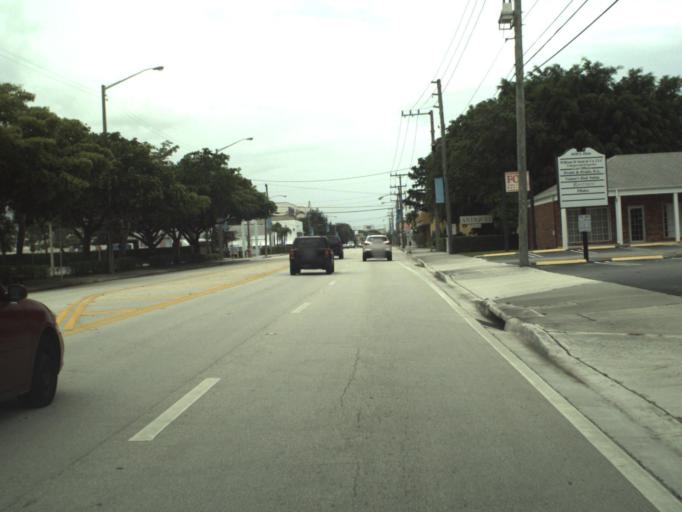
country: US
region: Florida
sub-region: Palm Beach County
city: Palm Beach
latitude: 26.6854
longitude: -80.0544
